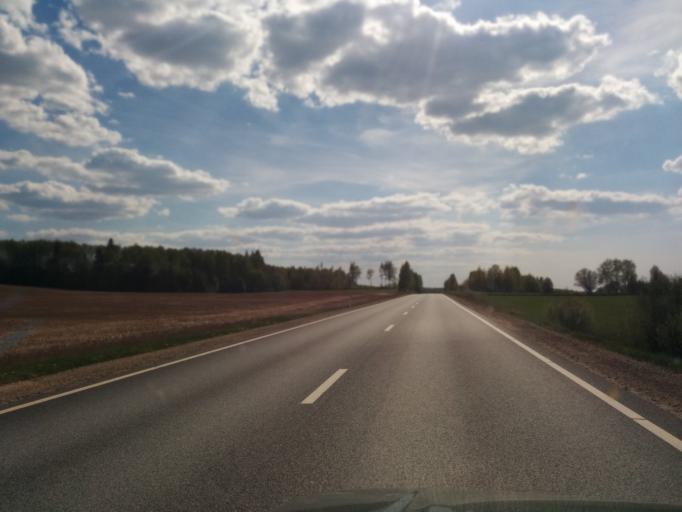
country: LV
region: Sigulda
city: Sigulda
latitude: 57.2472
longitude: 24.8457
